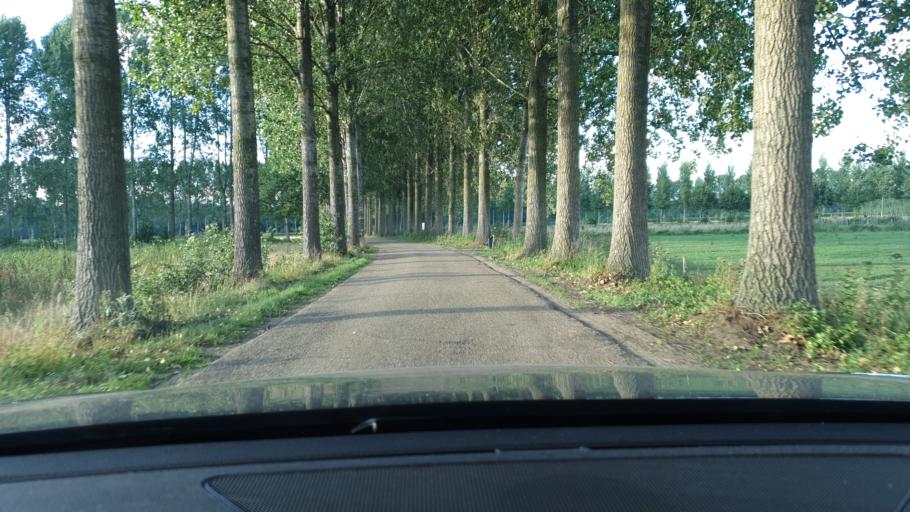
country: NL
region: North Brabant
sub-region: Gemeente Best
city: Best
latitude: 51.5307
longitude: 5.3936
